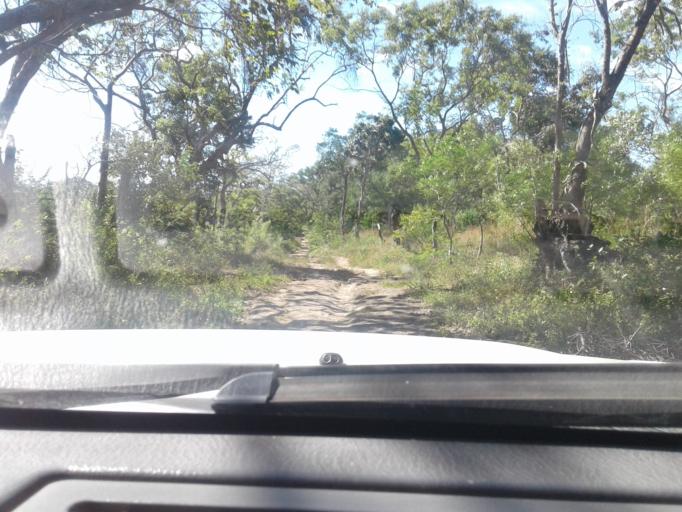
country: NI
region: Carazo
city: Santa Teresa
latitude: 11.7760
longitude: -86.1874
